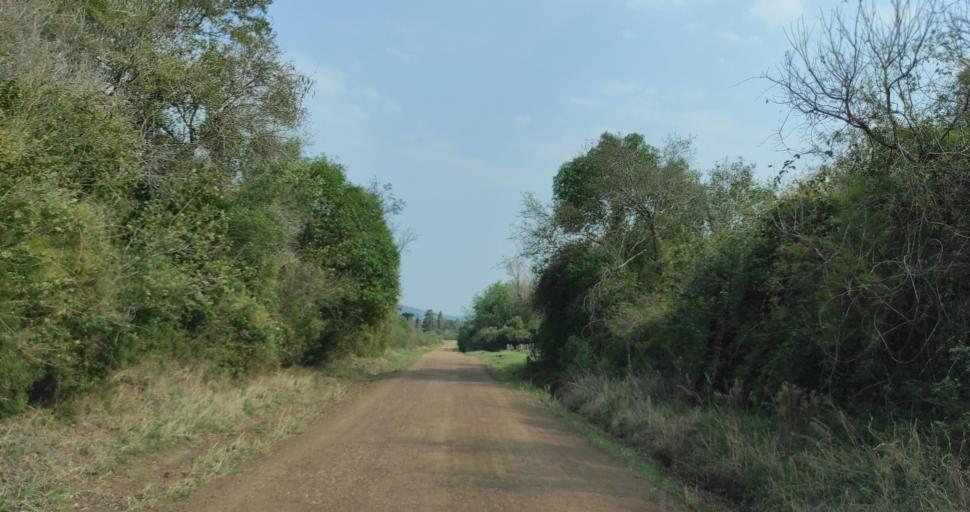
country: AR
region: Misiones
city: Cerro Cora
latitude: -27.5613
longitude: -55.5826
